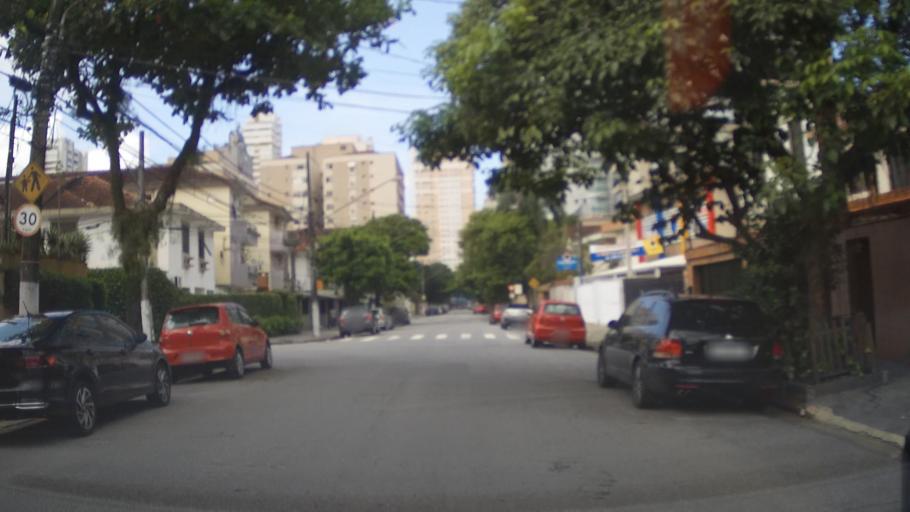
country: BR
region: Sao Paulo
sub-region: Santos
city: Santos
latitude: -23.9618
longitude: -46.3265
